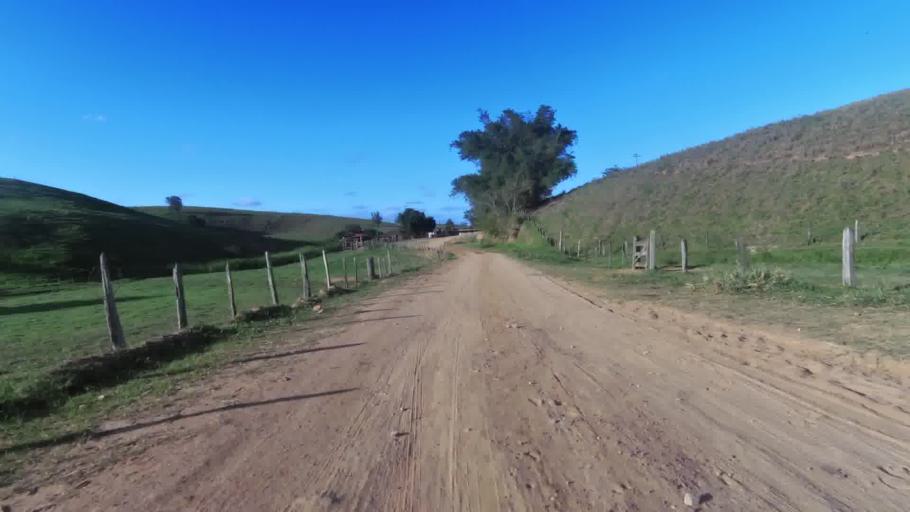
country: BR
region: Espirito Santo
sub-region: Marataizes
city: Marataizes
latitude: -21.1492
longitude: -41.0328
